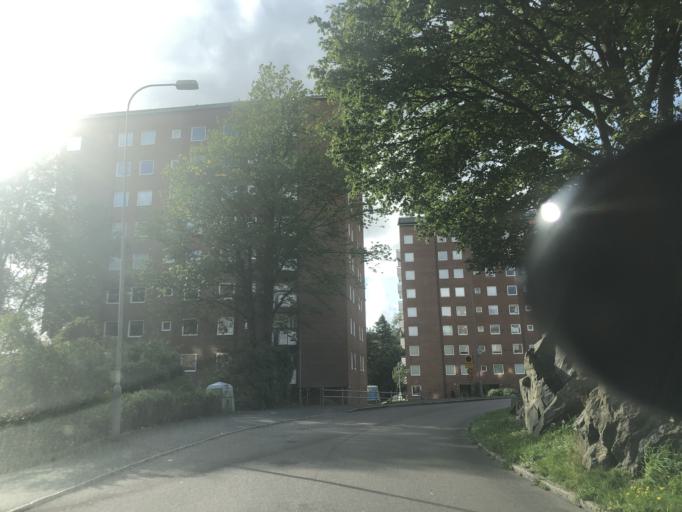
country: SE
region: Vaestra Goetaland
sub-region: Goteborg
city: Goeteborg
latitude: 57.7291
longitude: 11.9721
